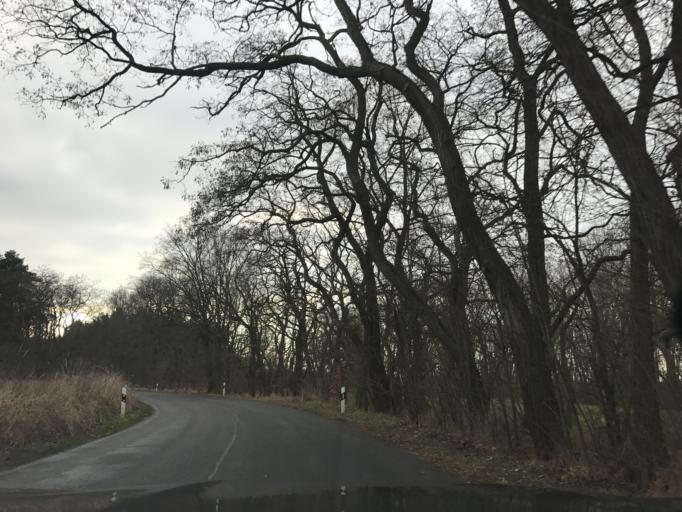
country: DE
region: Brandenburg
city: Brandenburg an der Havel
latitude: 52.3620
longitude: 12.5441
